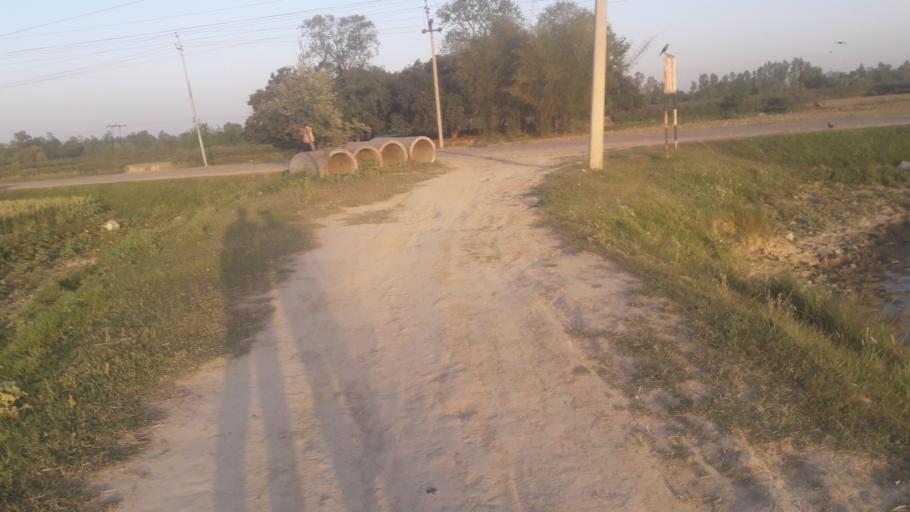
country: NP
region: Eastern Region
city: Siraha
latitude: 26.6315
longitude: 86.1962
